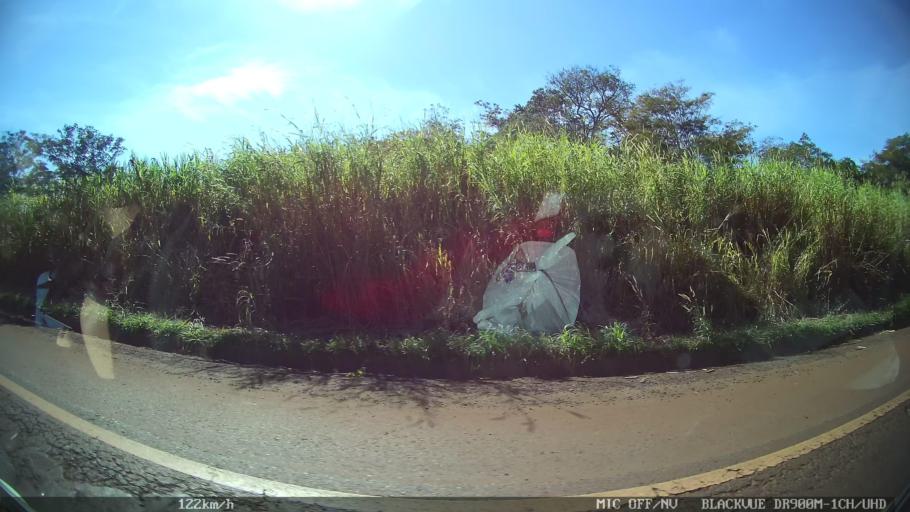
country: BR
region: Sao Paulo
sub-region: Ipua
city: Ipua
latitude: -20.4508
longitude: -48.1762
